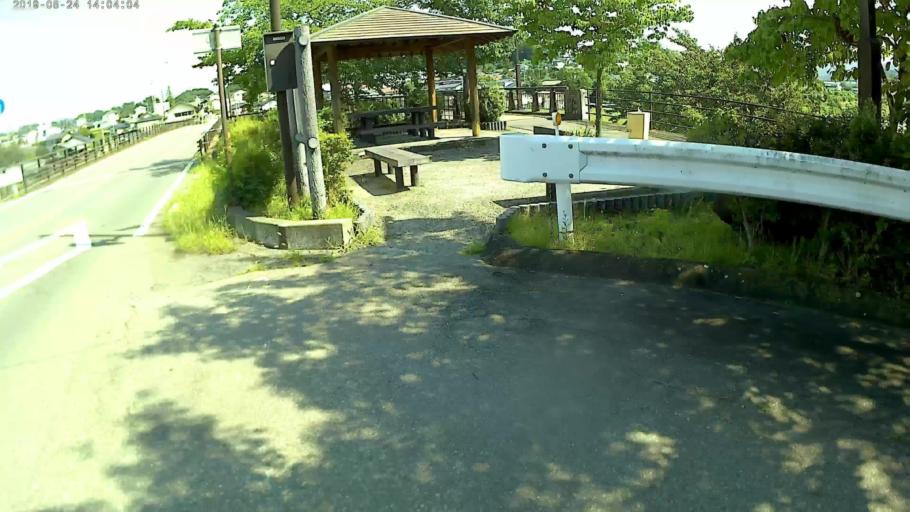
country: JP
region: Nagano
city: Komoro
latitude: 36.2712
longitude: 138.4171
